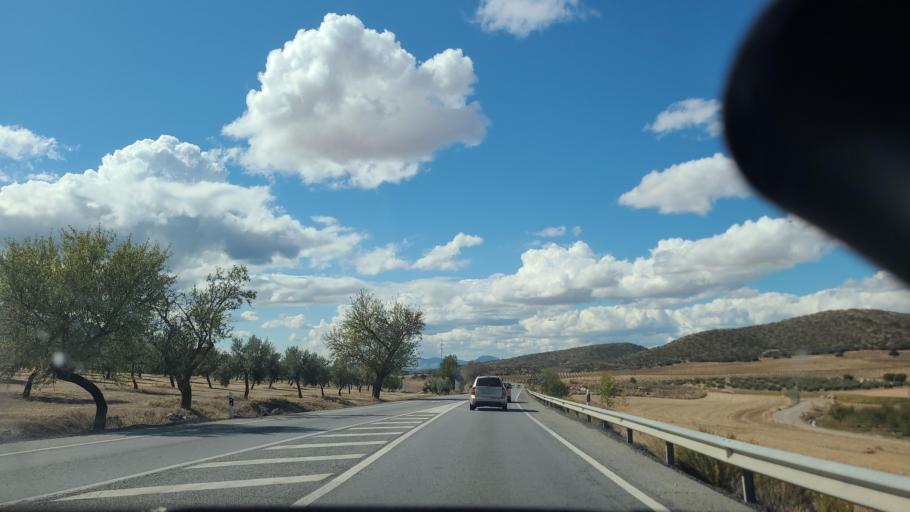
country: ES
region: Andalusia
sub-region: Provincia de Granada
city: Pinar
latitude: 37.4062
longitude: -3.3811
